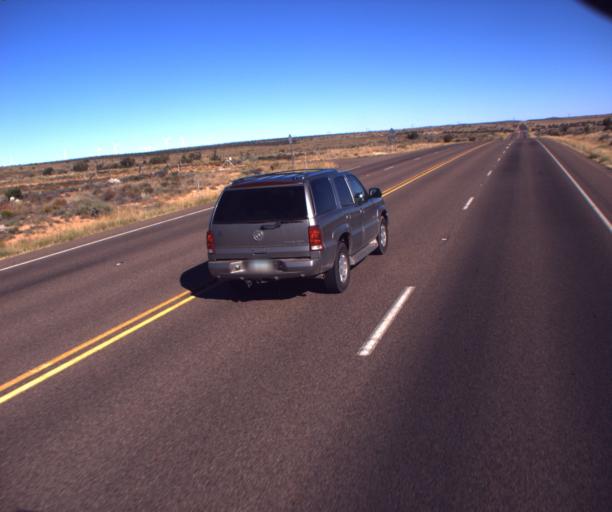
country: US
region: Arizona
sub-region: Navajo County
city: Snowflake
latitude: 34.5787
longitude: -110.0839
